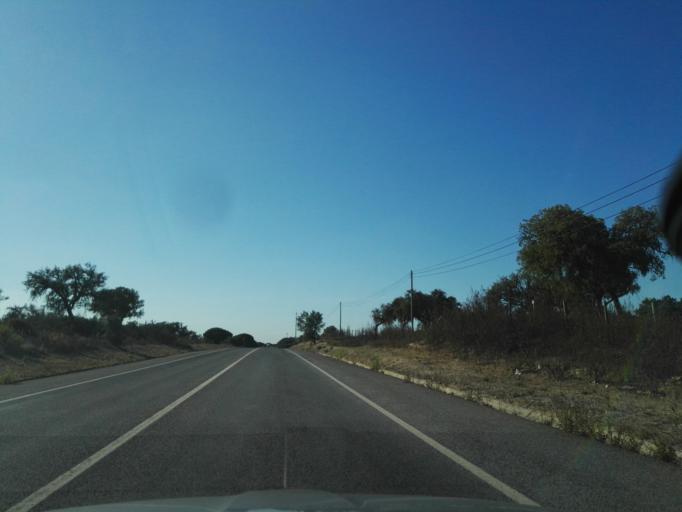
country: PT
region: Santarem
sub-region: Benavente
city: Poceirao
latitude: 38.8401
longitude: -8.7389
